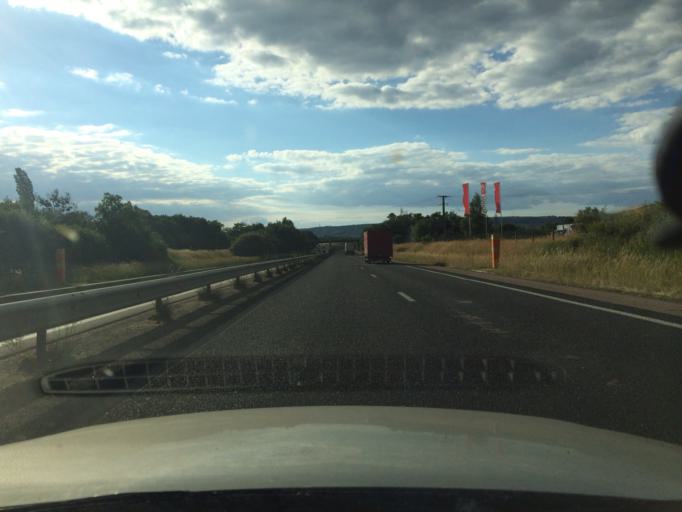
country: FR
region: Lorraine
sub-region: Departement de Meurthe-et-Moselle
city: Domgermain
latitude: 48.6611
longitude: 5.8345
